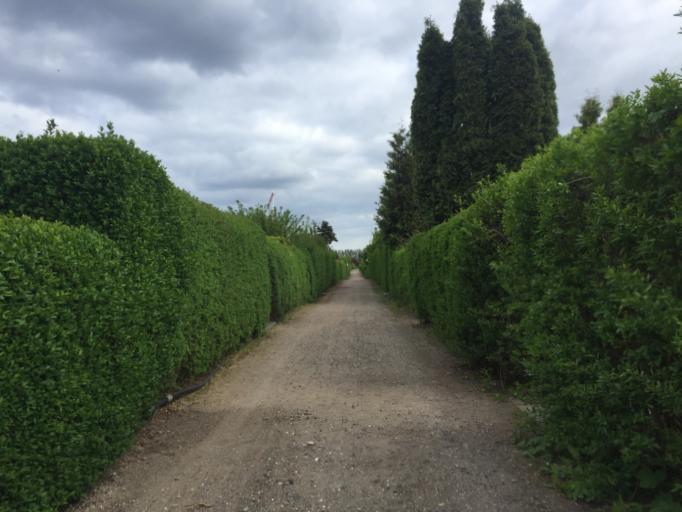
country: DK
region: Capital Region
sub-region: Kobenhavn
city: Christianshavn
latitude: 55.6811
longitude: 12.6145
